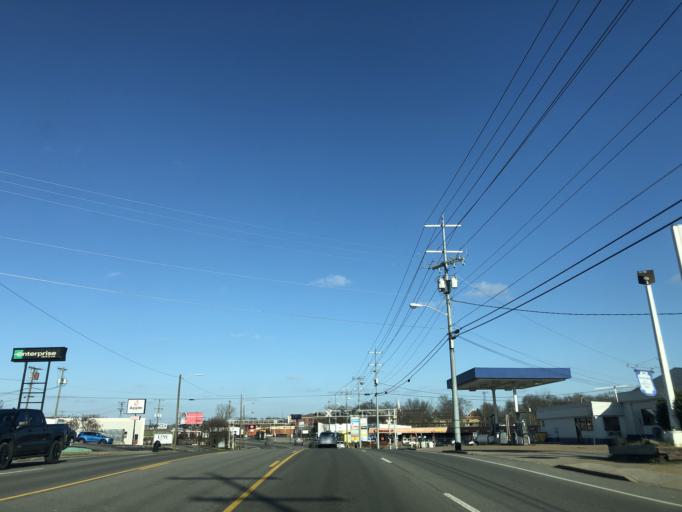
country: US
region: Tennessee
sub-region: Sumner County
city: Gallatin
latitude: 36.3851
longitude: -86.4550
